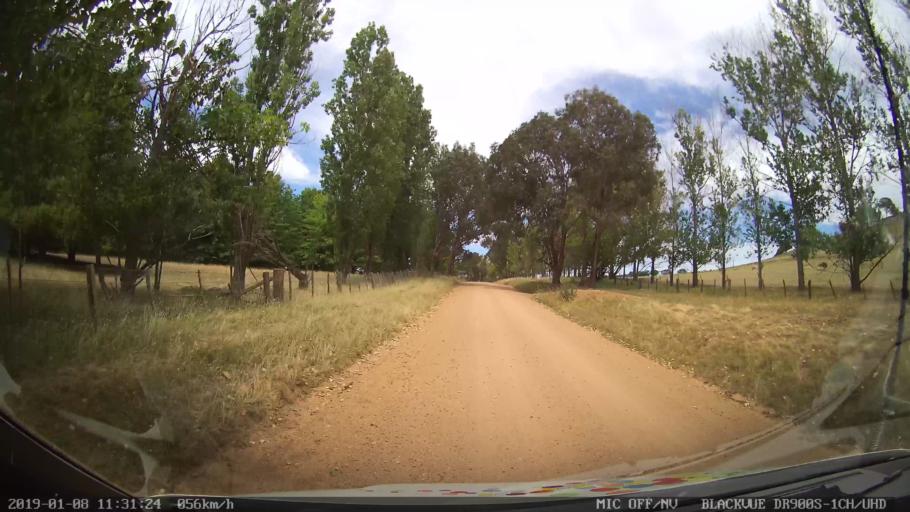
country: AU
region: New South Wales
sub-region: Guyra
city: Guyra
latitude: -30.3123
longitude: 151.5374
